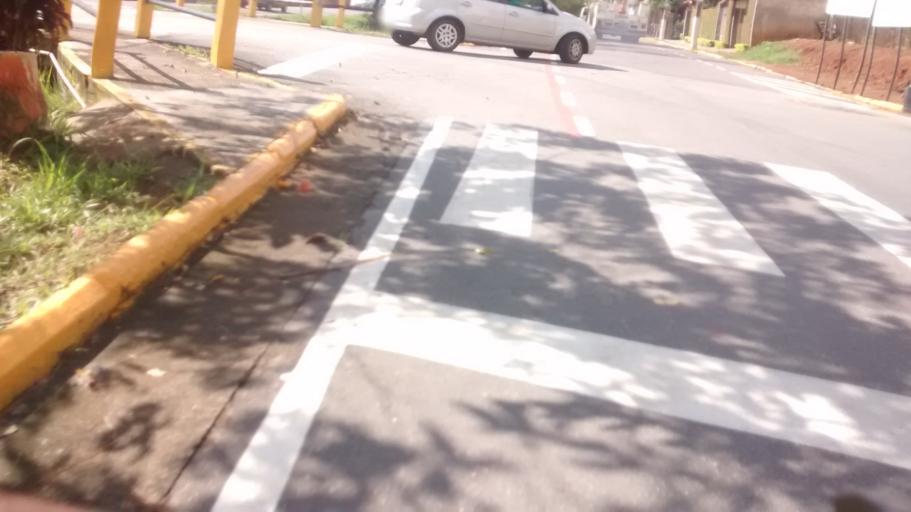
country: BR
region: Minas Gerais
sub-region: Itajuba
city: Itajuba
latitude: -22.4144
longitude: -45.4535
